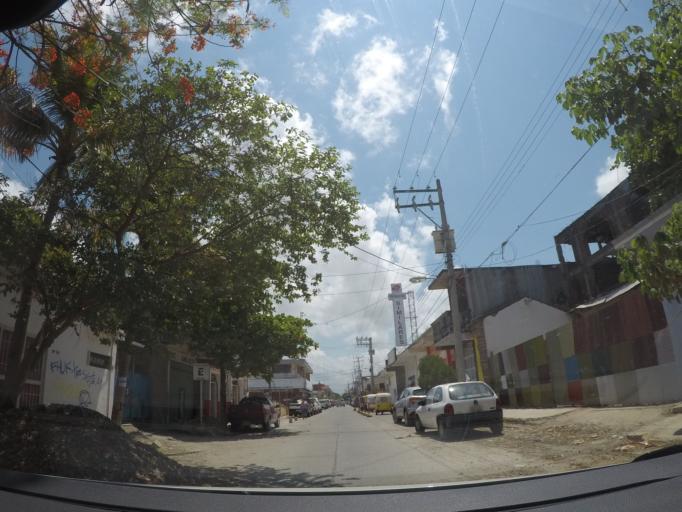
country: MX
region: Oaxaca
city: Juchitan de Zaragoza
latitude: 16.4338
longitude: -95.0192
